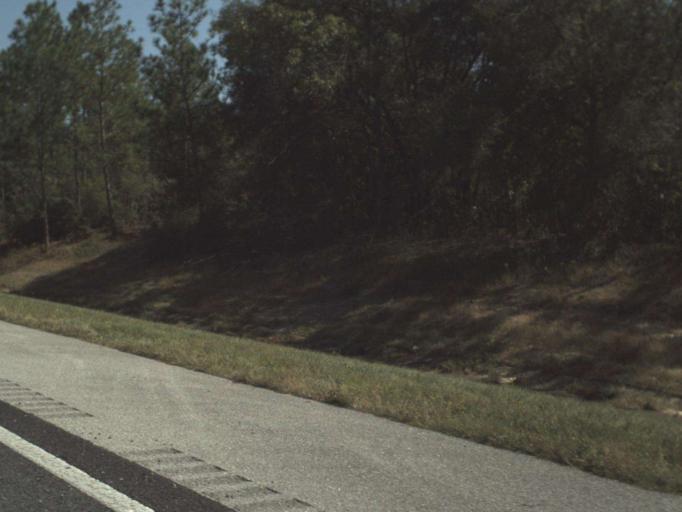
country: US
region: Florida
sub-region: Okaloosa County
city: Crestview
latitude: 30.7143
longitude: -86.6911
